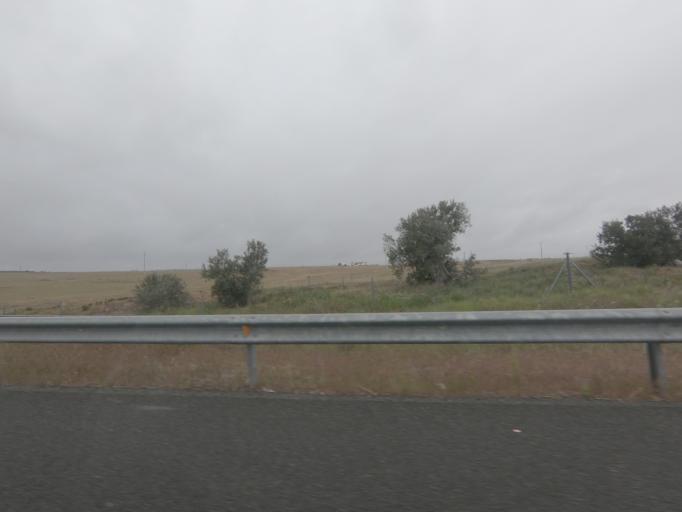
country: ES
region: Extremadura
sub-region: Provincia de Caceres
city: Casar de Caceres
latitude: 39.5550
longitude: -6.4013
